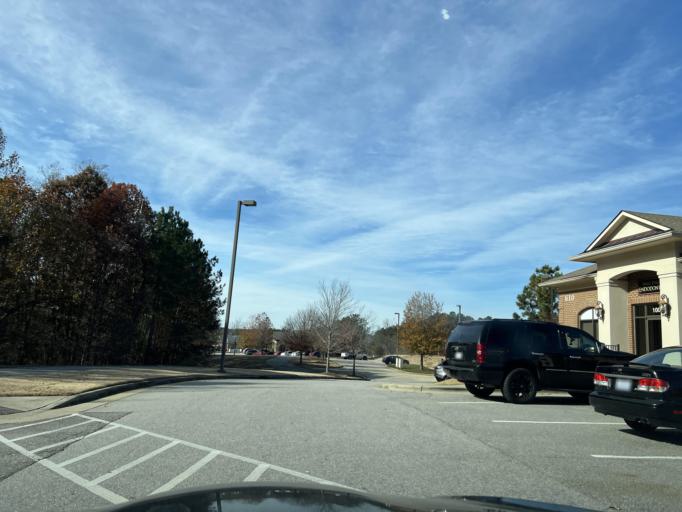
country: US
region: North Carolina
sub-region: Wake County
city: Wake Forest
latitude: 35.9663
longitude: -78.5226
